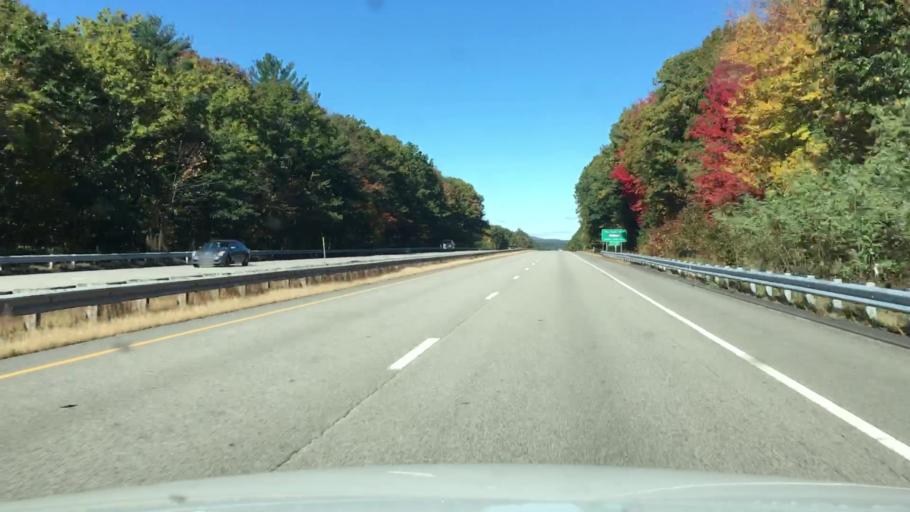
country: US
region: New Hampshire
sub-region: Strafford County
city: Rochester
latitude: 43.2622
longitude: -70.9493
